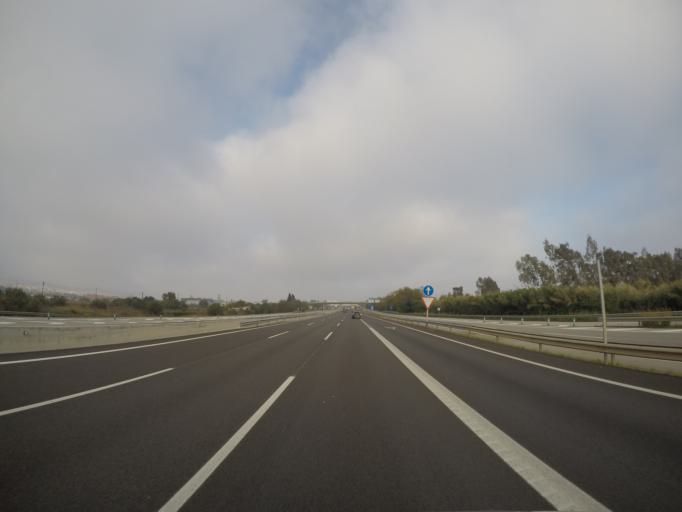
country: ES
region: Catalonia
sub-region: Provincia de Barcelona
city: Gava
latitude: 41.2892
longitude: 2.0040
